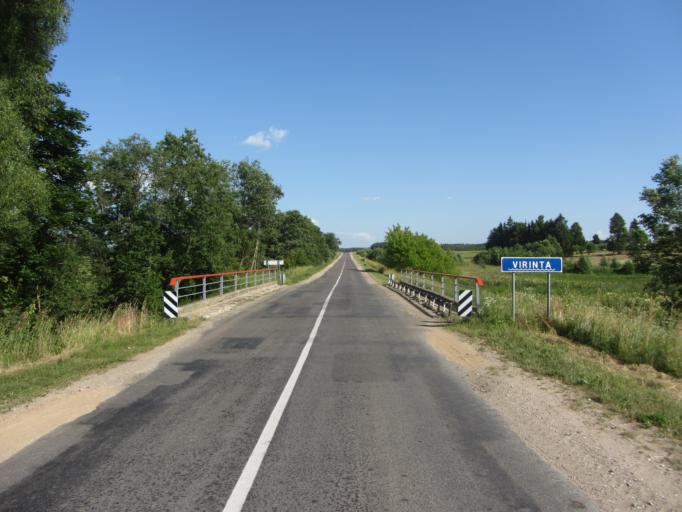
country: LT
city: Moletai
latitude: 55.3403
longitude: 25.3086
